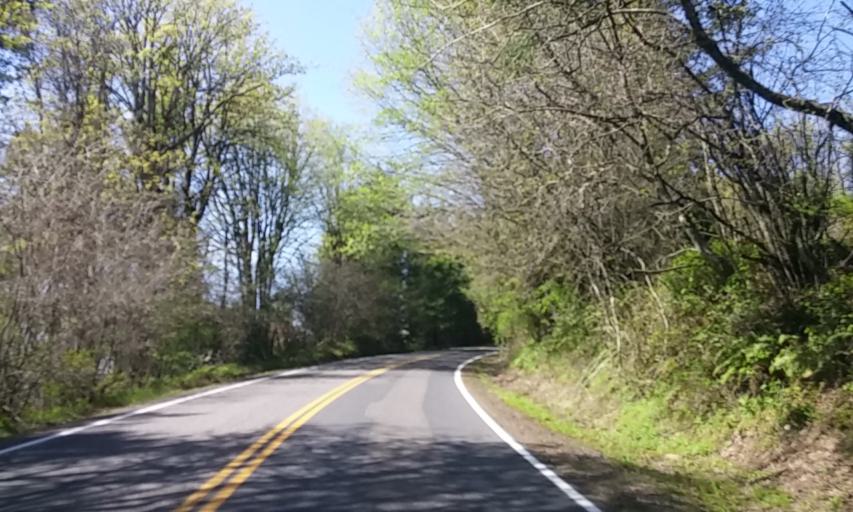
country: US
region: Oregon
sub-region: Washington County
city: West Haven
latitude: 45.5326
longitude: -122.7565
